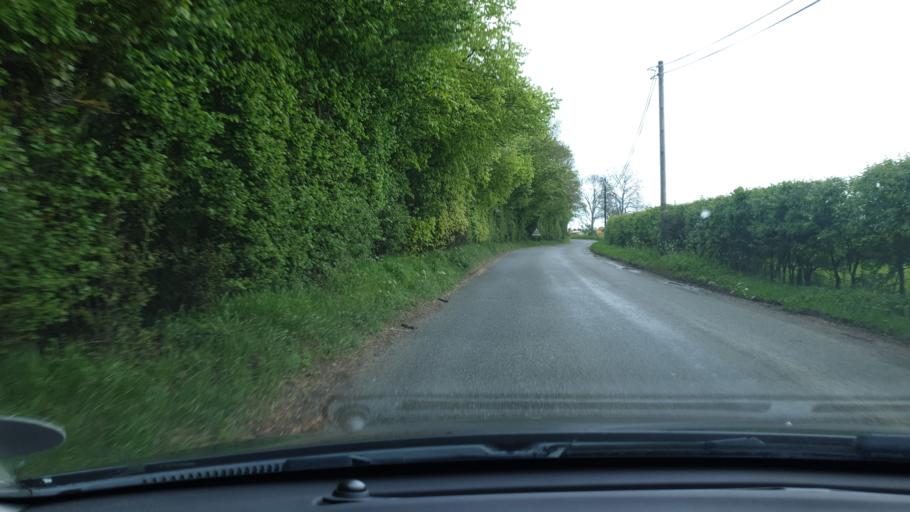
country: GB
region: England
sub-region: Essex
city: Great Bentley
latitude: 51.8765
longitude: 1.0819
